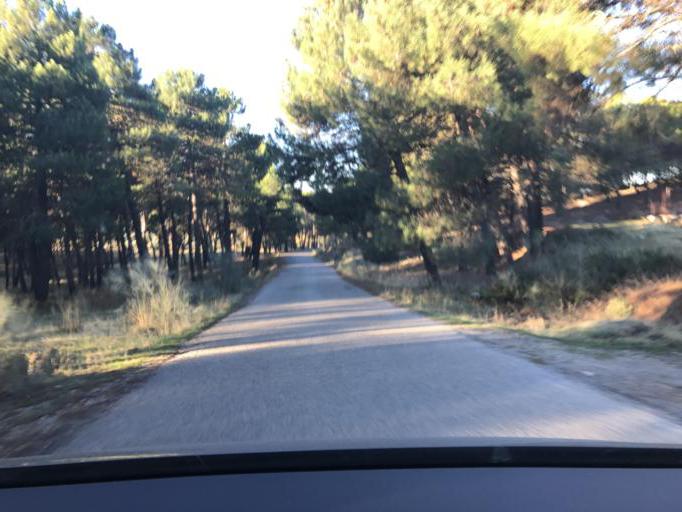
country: ES
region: Andalusia
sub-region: Provincia de Granada
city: Viznar
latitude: 37.2360
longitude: -3.5436
